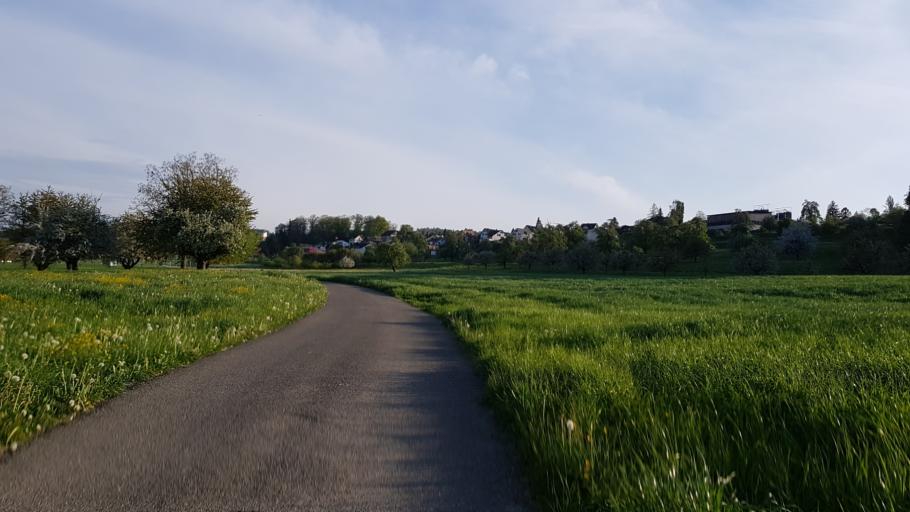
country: CH
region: Aargau
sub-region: Bezirk Kulm
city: Reinach
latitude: 47.2739
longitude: 8.2075
